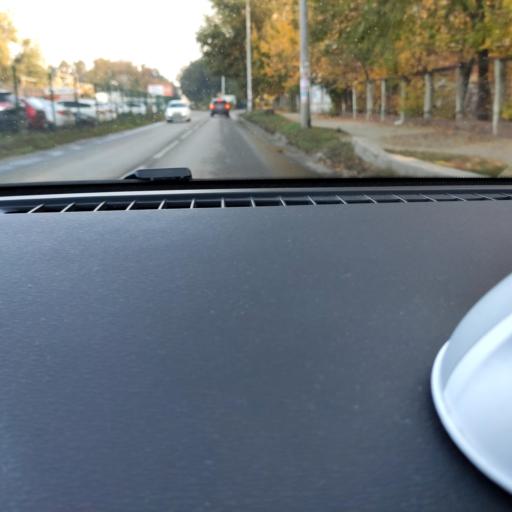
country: RU
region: Samara
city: Petra-Dubrava
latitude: 53.2379
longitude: 50.2747
